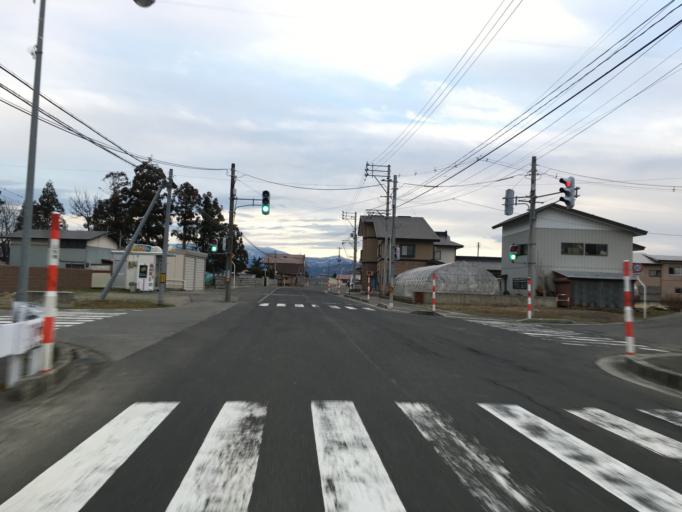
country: JP
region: Yamagata
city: Yonezawa
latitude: 37.9910
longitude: 140.0760
